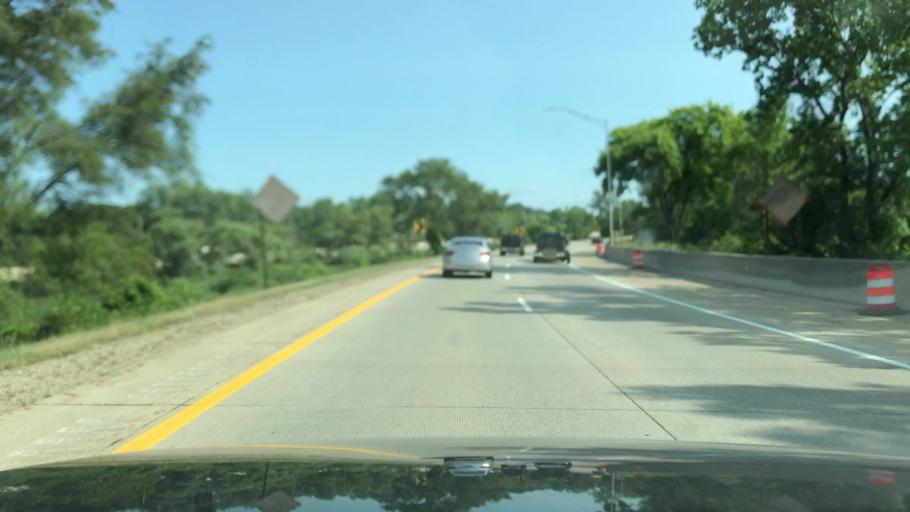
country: US
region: Michigan
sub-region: Kent County
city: Comstock Park
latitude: 43.0130
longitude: -85.6746
